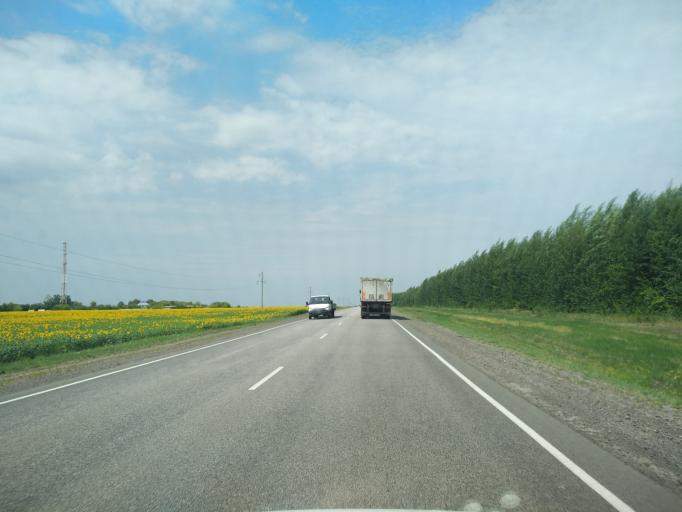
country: RU
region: Voronezj
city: Orlovo
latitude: 51.6764
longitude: 39.7044
